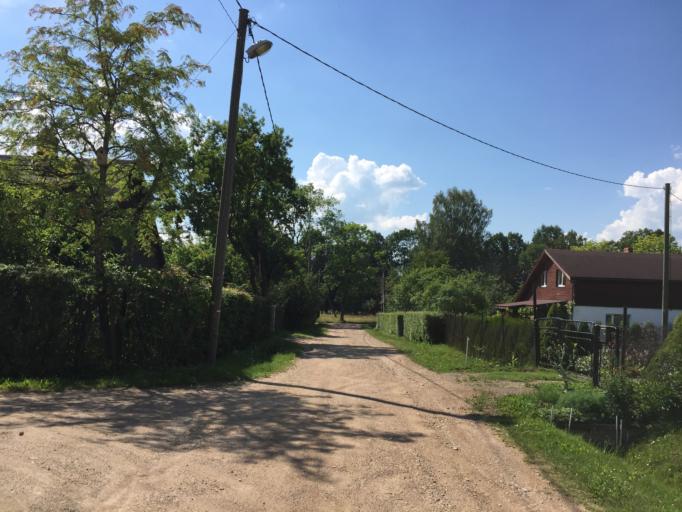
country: LV
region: Sigulda
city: Sigulda
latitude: 57.1459
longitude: 24.8400
